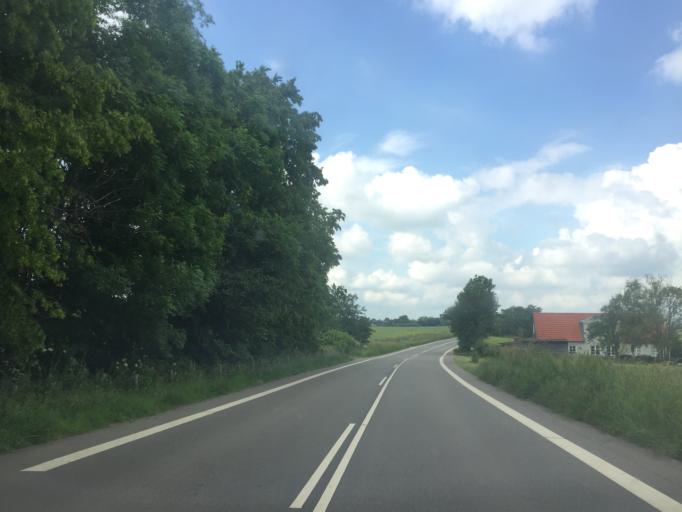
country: DK
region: Zealand
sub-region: Roskilde Kommune
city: Gundsomagle
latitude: 55.6979
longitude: 12.1601
